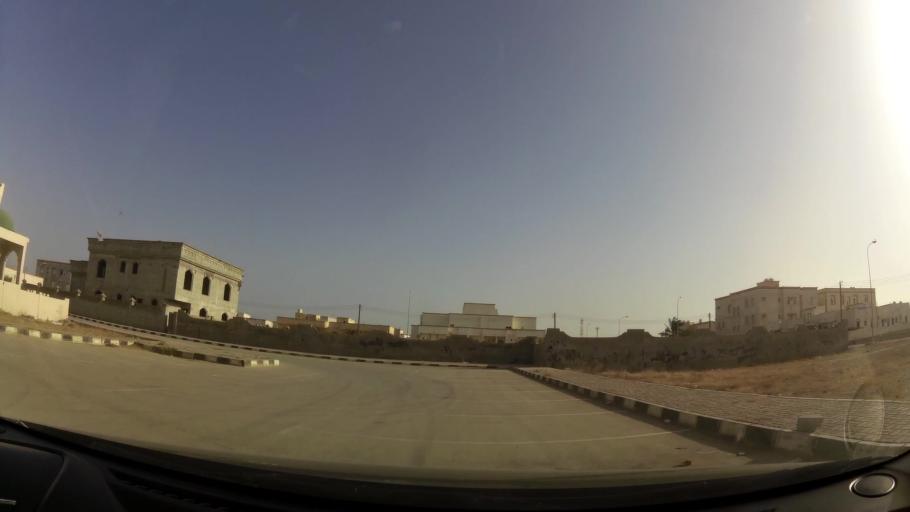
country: OM
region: Zufar
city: Salalah
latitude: 17.0208
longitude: 54.0227
